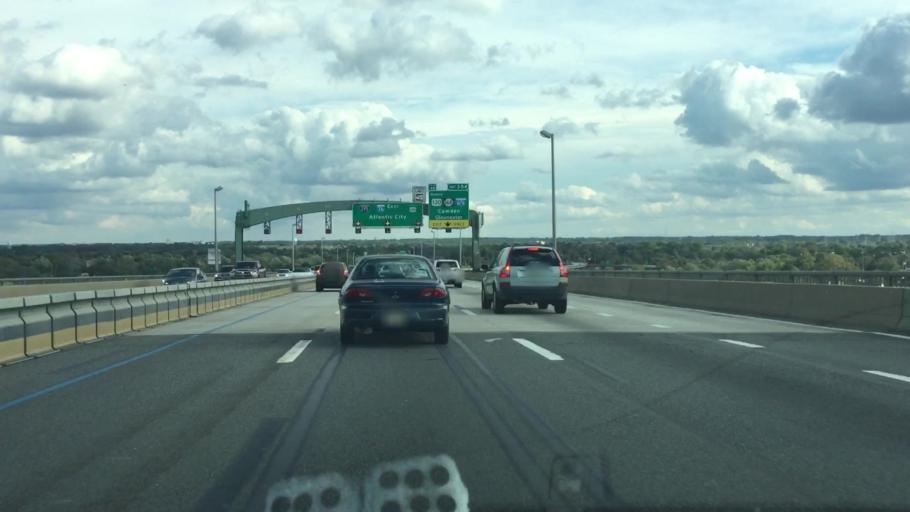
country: US
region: New Jersey
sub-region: Camden County
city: Gloucester City
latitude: 39.9039
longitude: -75.1219
